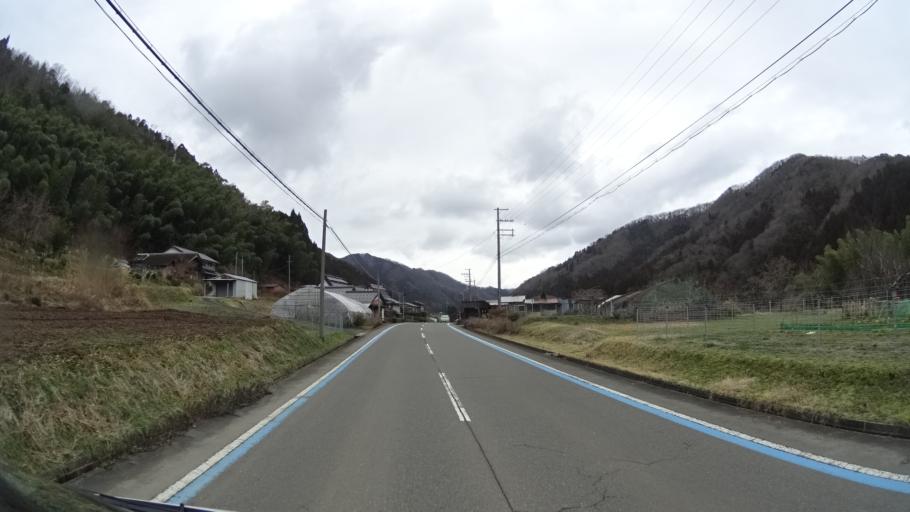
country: JP
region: Kyoto
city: Maizuru
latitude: 35.3833
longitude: 135.4177
